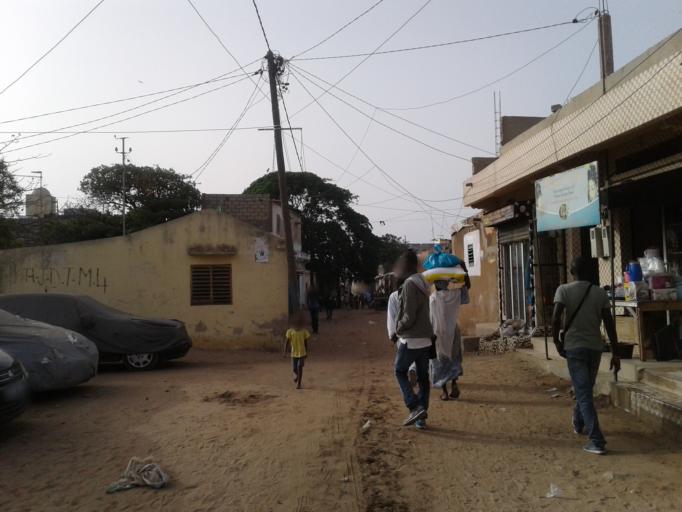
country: SN
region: Dakar
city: Pikine
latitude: 14.7654
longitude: -17.3794
